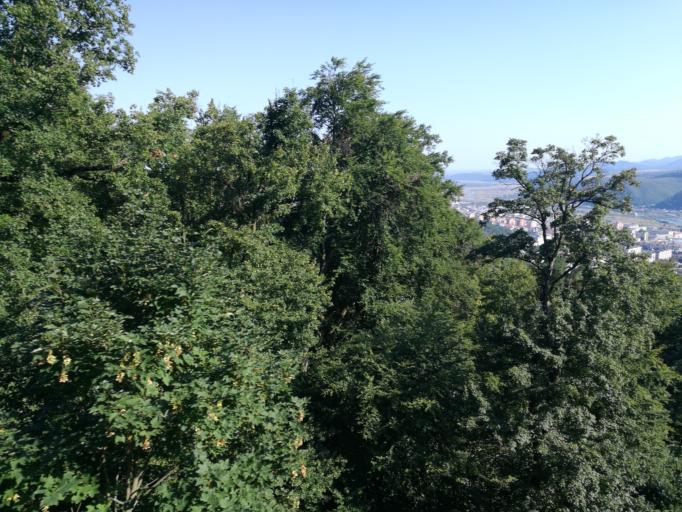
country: RO
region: Neamt
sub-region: Comuna Garcina
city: Garcina
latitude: 46.9414
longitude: 26.3660
